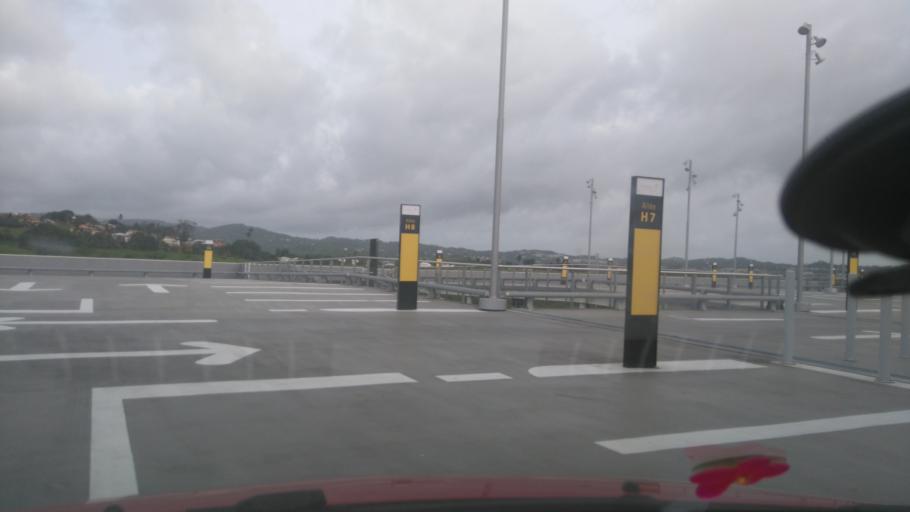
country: MQ
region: Martinique
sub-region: Martinique
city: Ducos
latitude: 14.5545
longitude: -60.9733
